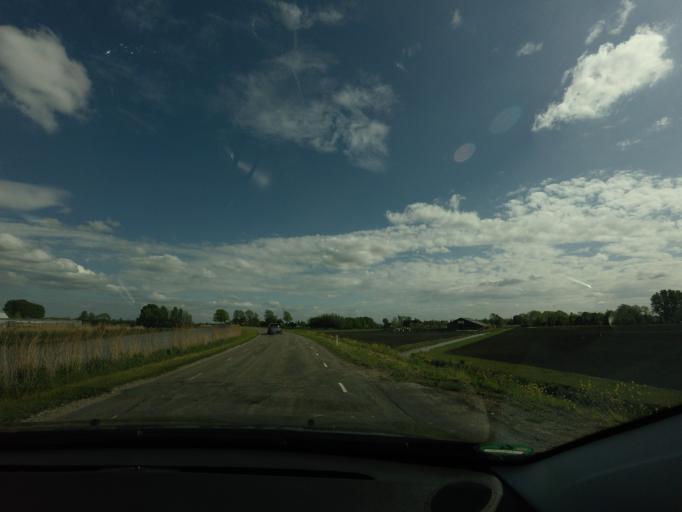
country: NL
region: North Holland
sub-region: Gemeente Heerhugowaard
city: Heerhugowaard
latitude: 52.6494
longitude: 4.8648
